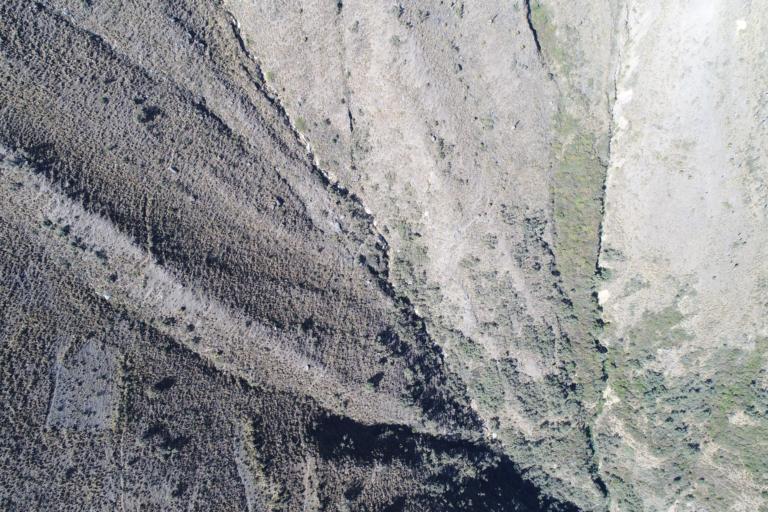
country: BO
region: La Paz
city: Viloco
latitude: -16.8090
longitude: -67.5560
